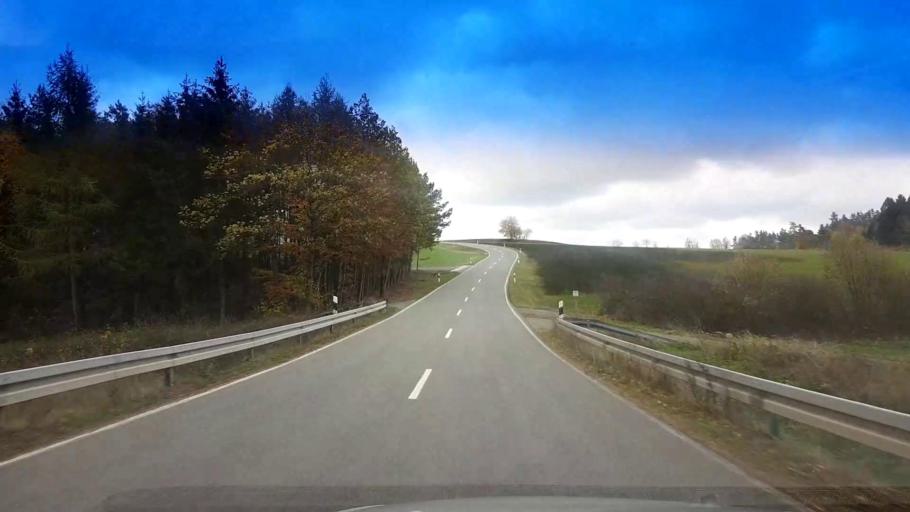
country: DE
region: Bavaria
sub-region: Upper Franconia
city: Poxdorf
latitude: 49.9428
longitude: 11.1074
